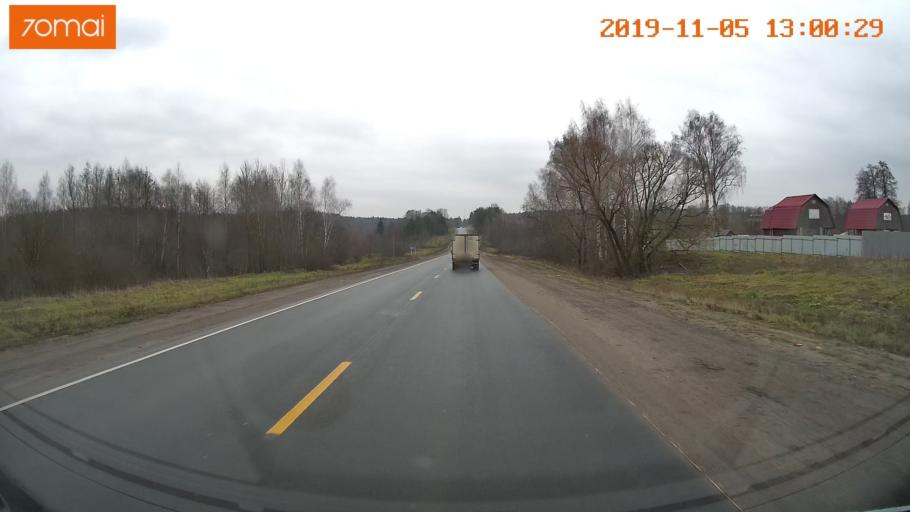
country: RU
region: Ivanovo
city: Kokhma
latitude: 56.9138
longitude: 41.1455
